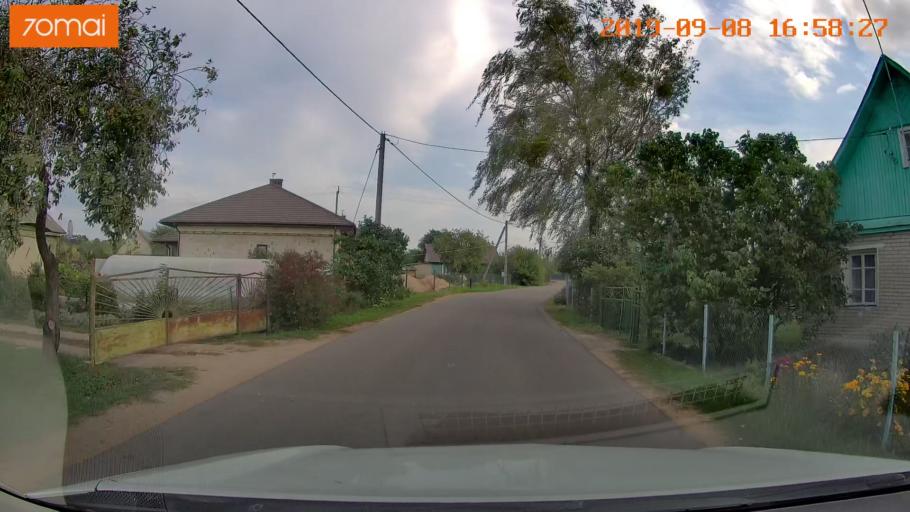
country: BY
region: Grodnenskaya
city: Hrodna
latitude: 53.7268
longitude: 23.9272
